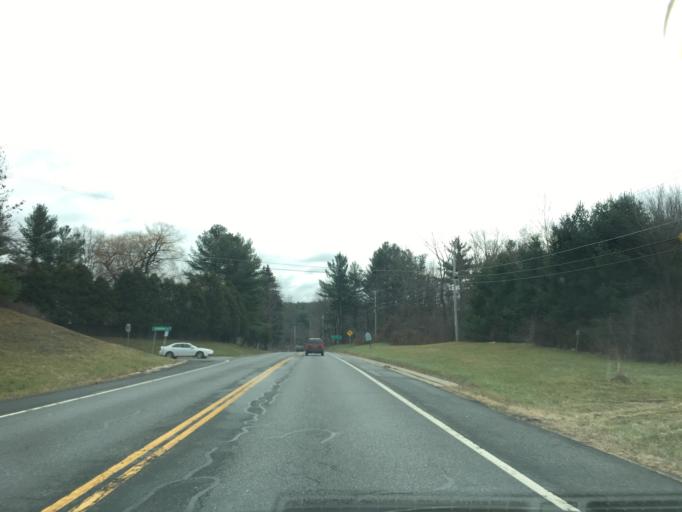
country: US
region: New York
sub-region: Rensselaer County
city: Averill Park
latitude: 42.6547
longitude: -73.5696
